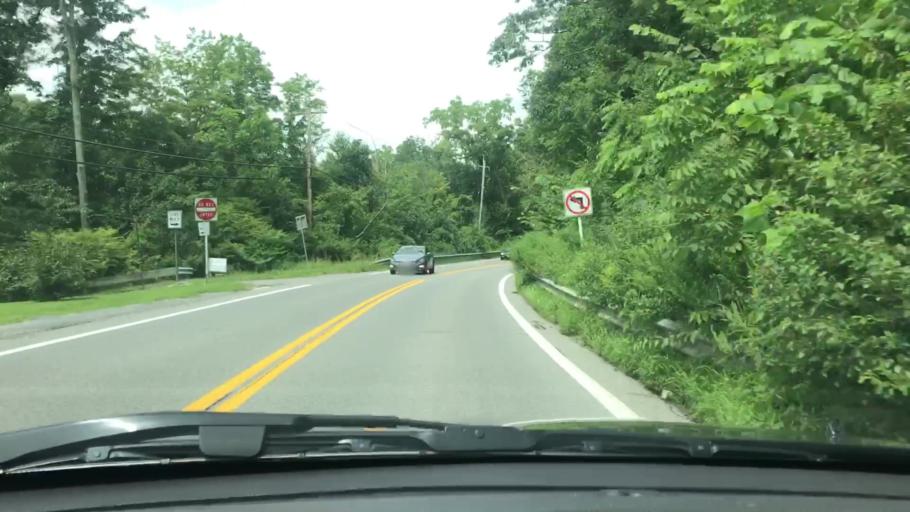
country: US
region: New York
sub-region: Westchester County
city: Bedford
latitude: 41.1947
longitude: -73.6240
